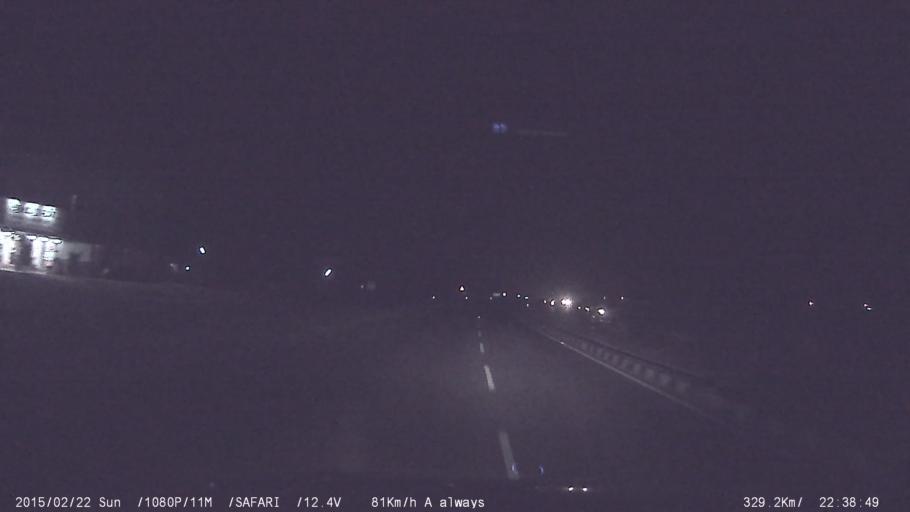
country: IN
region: Tamil Nadu
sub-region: Namakkal
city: Velur
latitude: 11.1698
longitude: 78.0384
